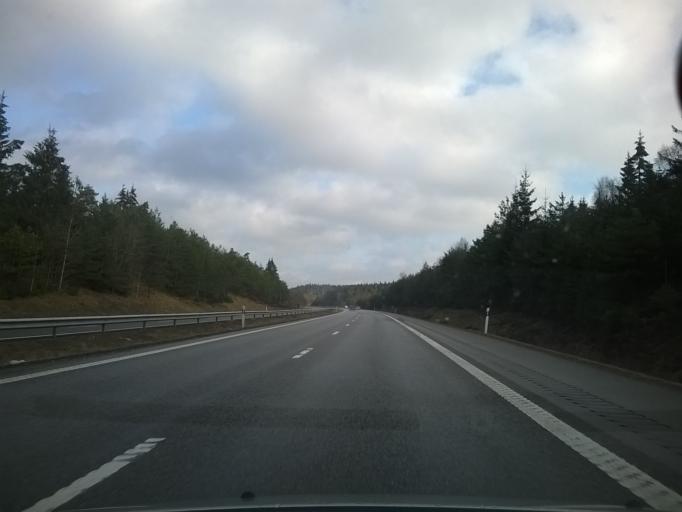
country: SE
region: Vaestra Goetaland
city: Svanesund
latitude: 58.1288
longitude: 11.8853
